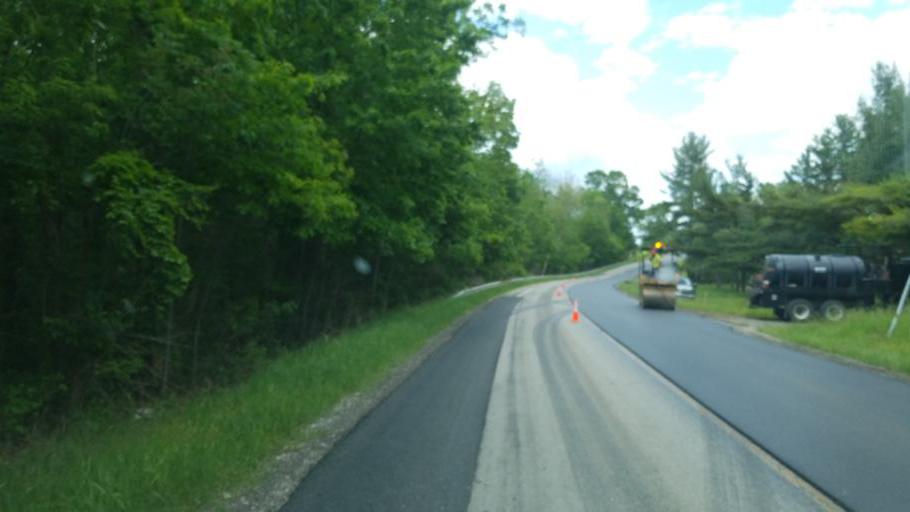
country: US
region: Ohio
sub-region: Erie County
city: Milan
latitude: 41.2980
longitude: -82.6356
